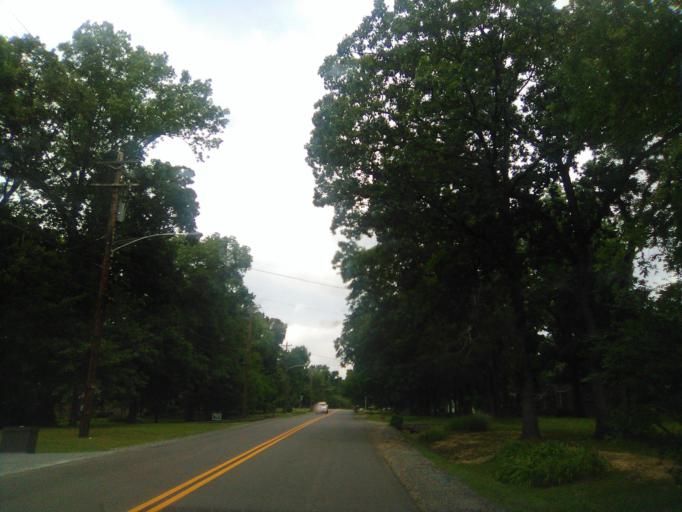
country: US
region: Tennessee
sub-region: Davidson County
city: Belle Meade
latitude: 36.1233
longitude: -86.8864
